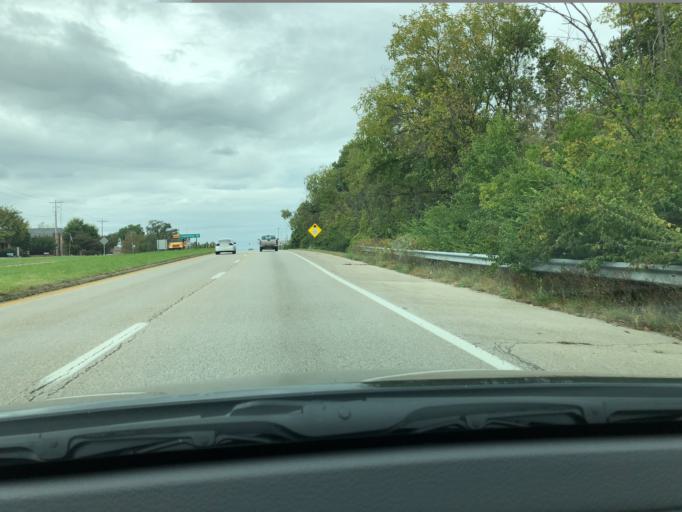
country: US
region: Ohio
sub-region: Franklin County
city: Minerva Park
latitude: 40.0814
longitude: -82.9342
